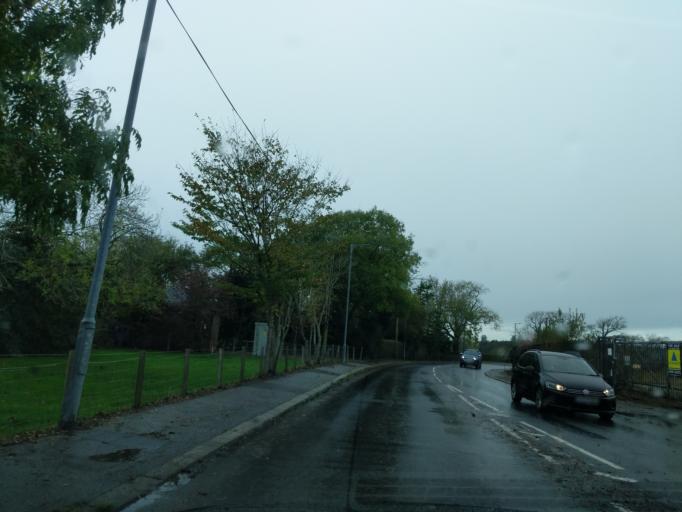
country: GB
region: Scotland
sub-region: Dumfries and Galloway
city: Kirkcudbright
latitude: 54.8395
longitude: -4.0523
